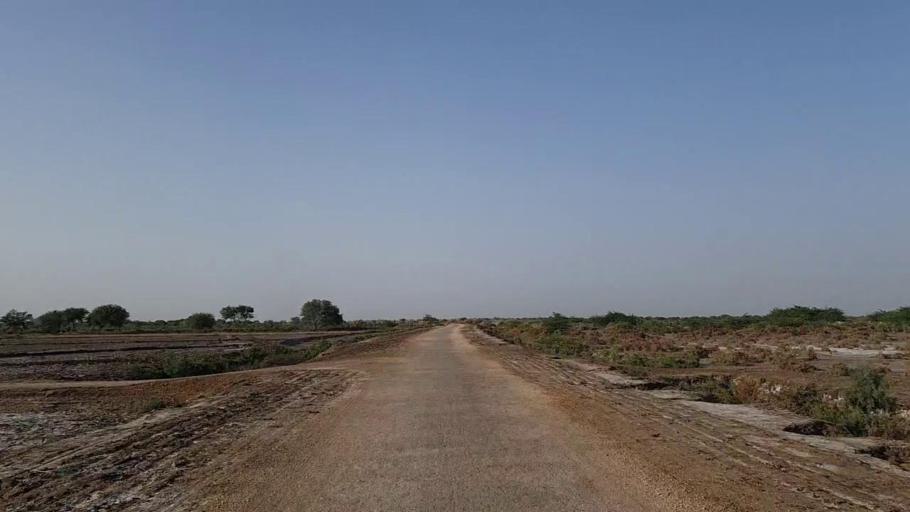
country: PK
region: Sindh
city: Jati
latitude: 24.3181
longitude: 68.1690
